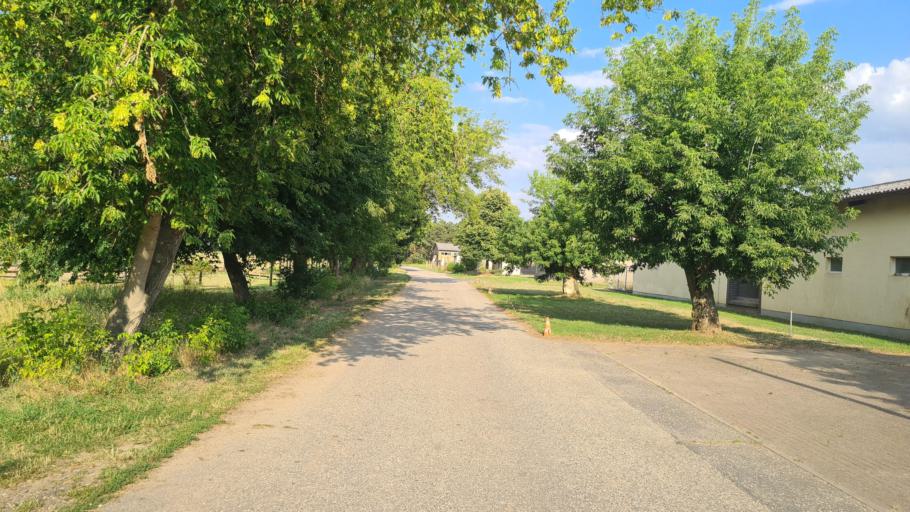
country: DE
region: Saxony-Anhalt
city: Pretzsch
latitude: 51.7635
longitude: 12.8362
